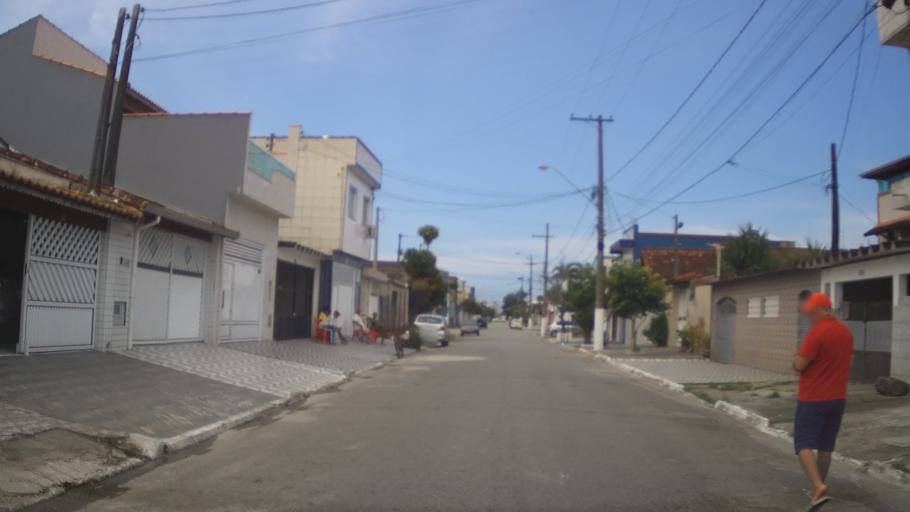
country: BR
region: Sao Paulo
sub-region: Praia Grande
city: Praia Grande
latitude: -24.0229
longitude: -46.4983
